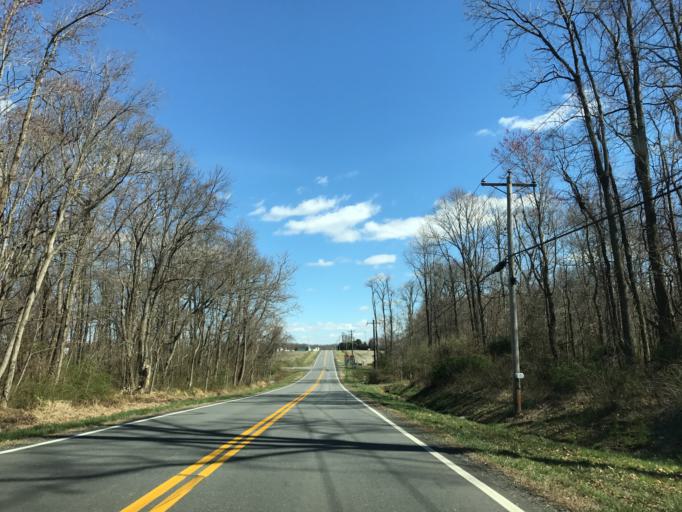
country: US
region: Maryland
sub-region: Queen Anne's County
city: Centreville
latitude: 39.0449
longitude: -76.0189
